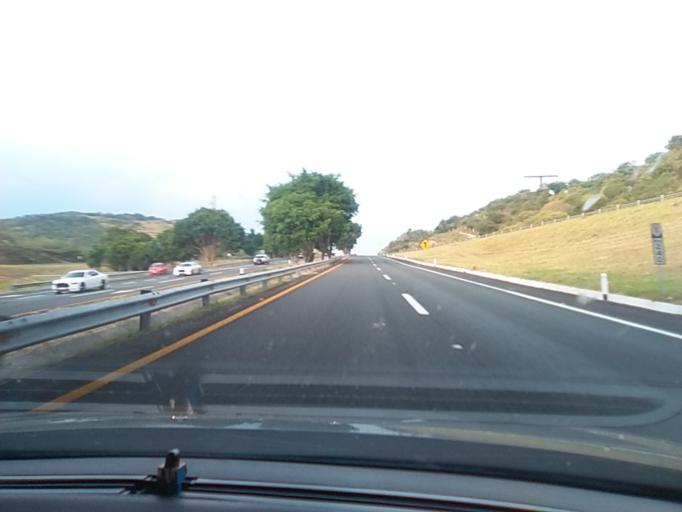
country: MX
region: Michoacan
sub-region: Cuitzeo
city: San Juan Benito Juarez (San Juan Tararameo)
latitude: 19.8974
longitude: -101.1465
